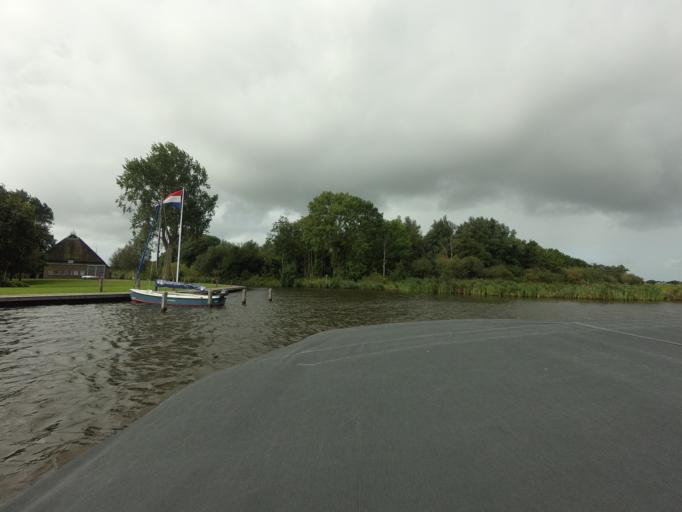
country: NL
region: Friesland
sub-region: Gemeente Boarnsterhim
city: Warten
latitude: 53.1393
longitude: 5.9135
